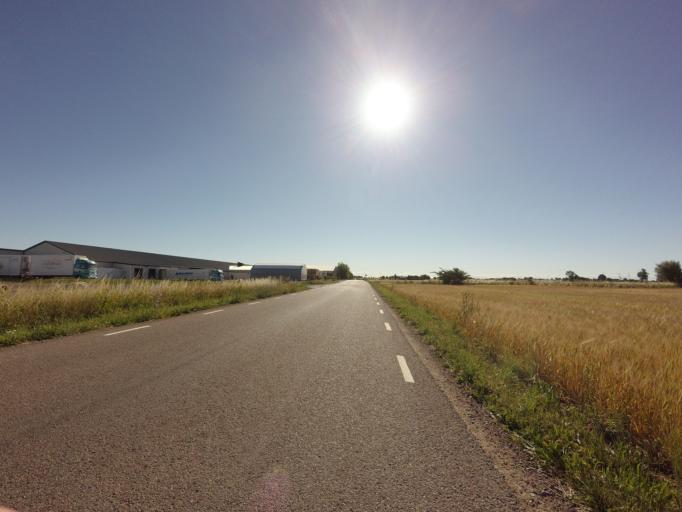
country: SE
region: Skane
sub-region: Trelleborgs Kommun
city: Skare
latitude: 55.4043
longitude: 13.0163
